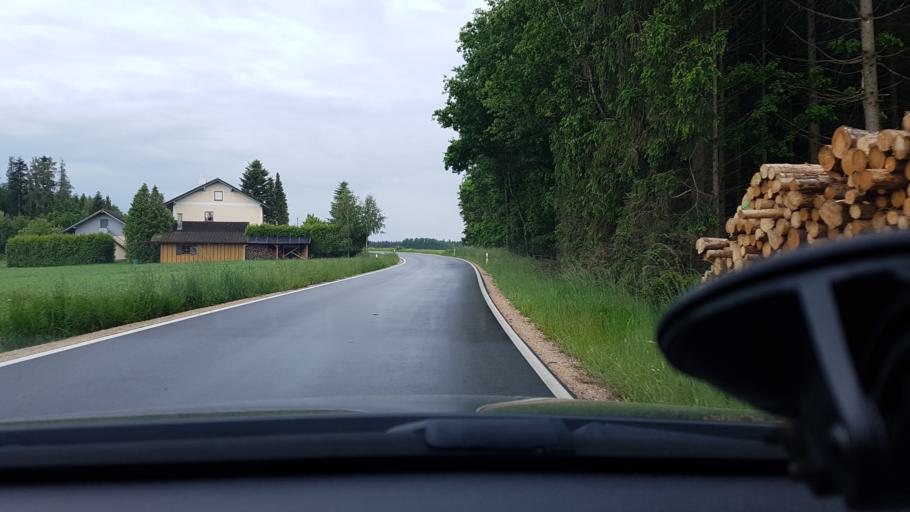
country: DE
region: Bavaria
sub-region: Lower Bavaria
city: Stubenberg
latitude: 48.3388
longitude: 13.0527
